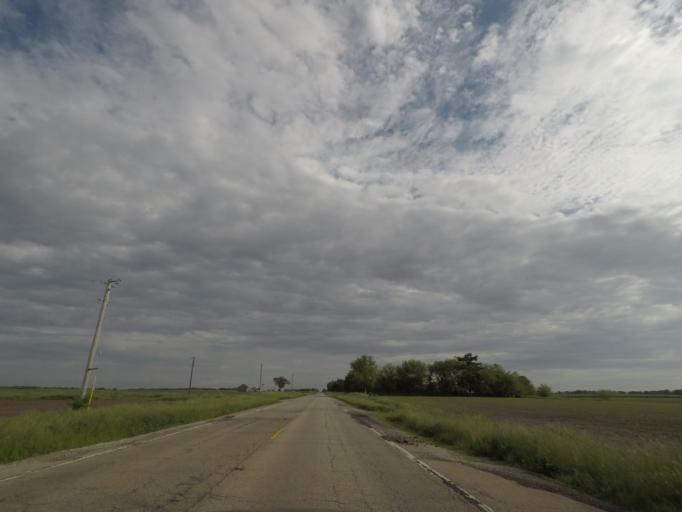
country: US
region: Illinois
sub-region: Logan County
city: Mount Pulaski
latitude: 40.0319
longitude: -89.2821
